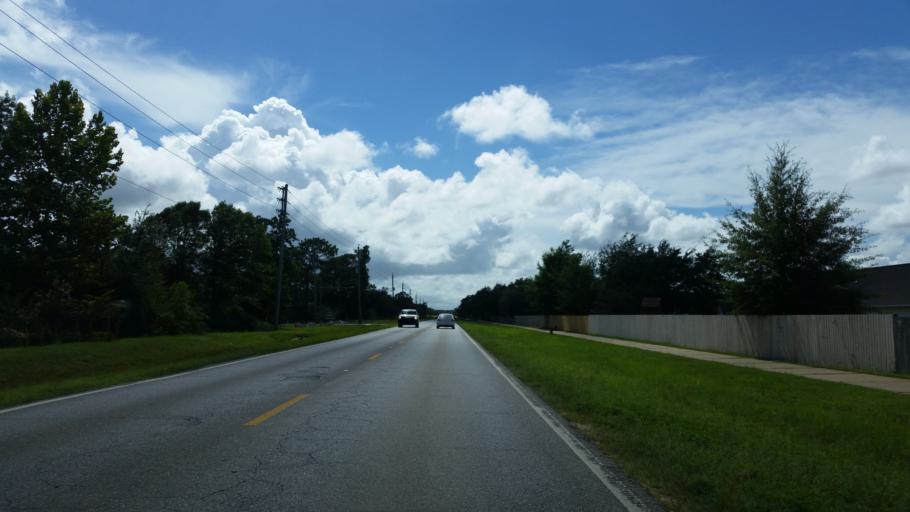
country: US
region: Florida
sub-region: Santa Rosa County
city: Holley
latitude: 30.4325
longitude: -86.8773
